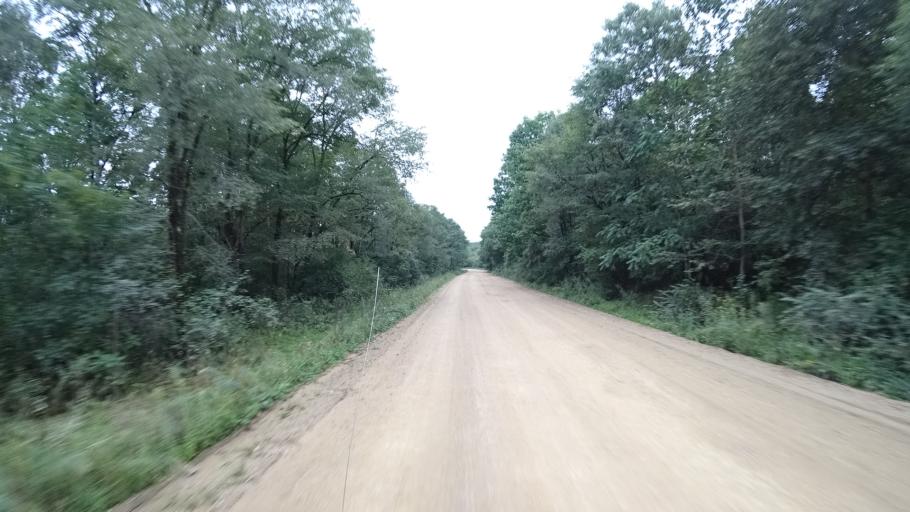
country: RU
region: Primorskiy
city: Rettikhovka
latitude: 44.1808
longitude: 132.8554
